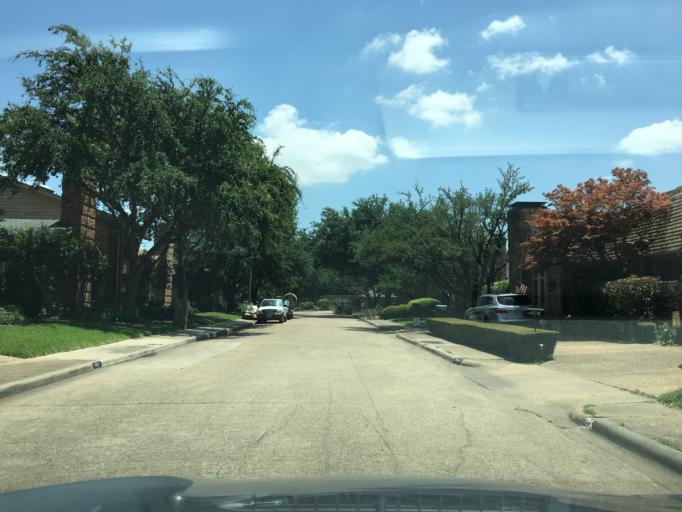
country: US
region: Texas
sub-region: Dallas County
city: University Park
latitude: 32.8923
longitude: -96.8068
